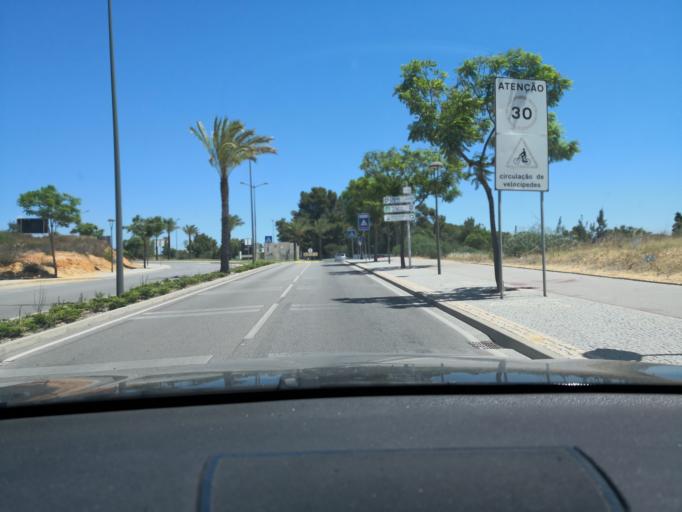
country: PT
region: Faro
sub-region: Albufeira
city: Albufeira
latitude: 37.0981
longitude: -8.2186
